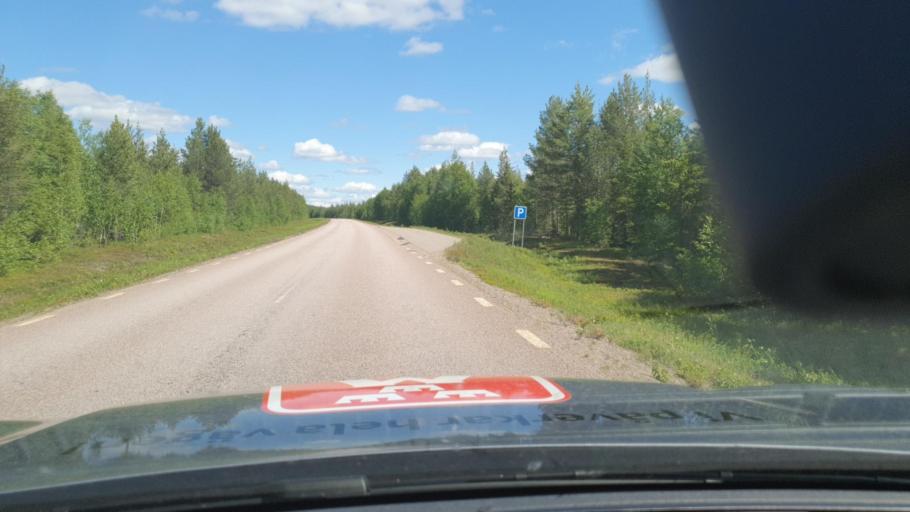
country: SE
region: Norrbotten
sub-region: Pajala Kommun
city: Pajala
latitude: 67.2076
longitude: 22.7776
